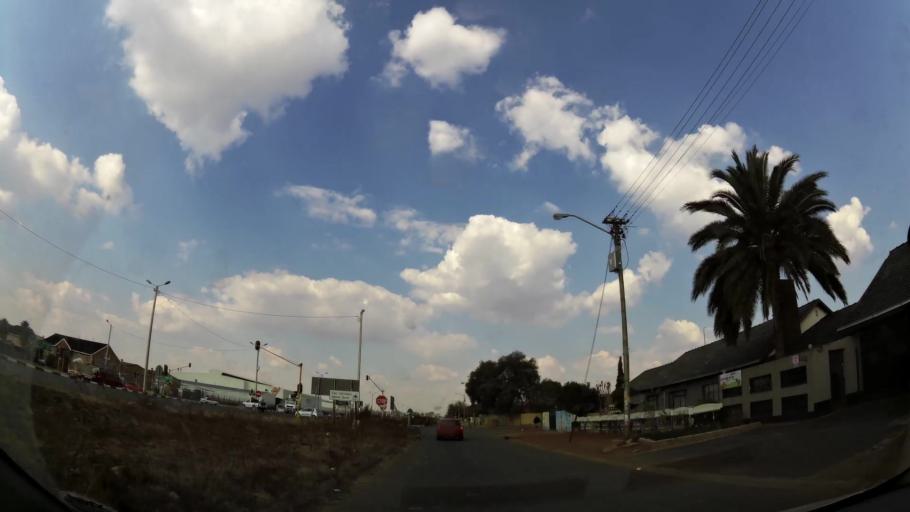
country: ZA
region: Gauteng
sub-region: Ekurhuleni Metropolitan Municipality
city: Germiston
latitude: -26.3079
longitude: 28.1968
